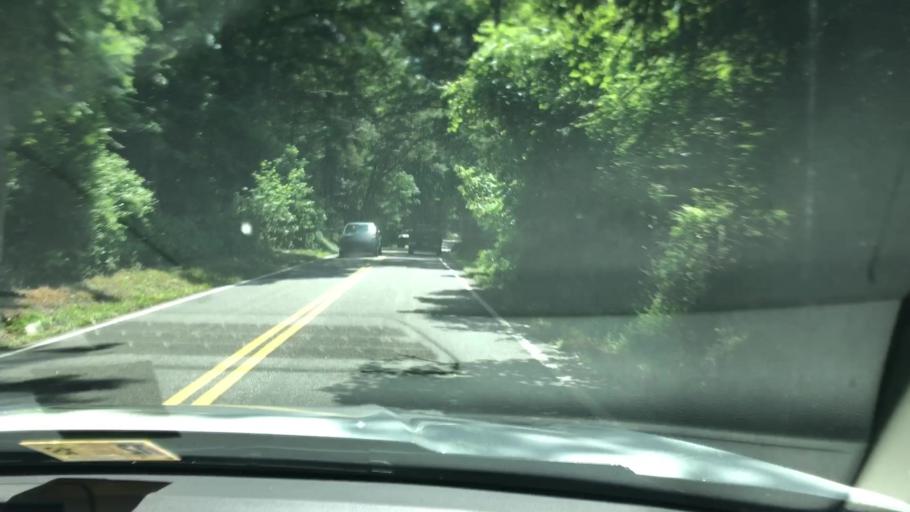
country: US
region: Virginia
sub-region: King William County
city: West Point
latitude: 37.4750
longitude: -76.8235
